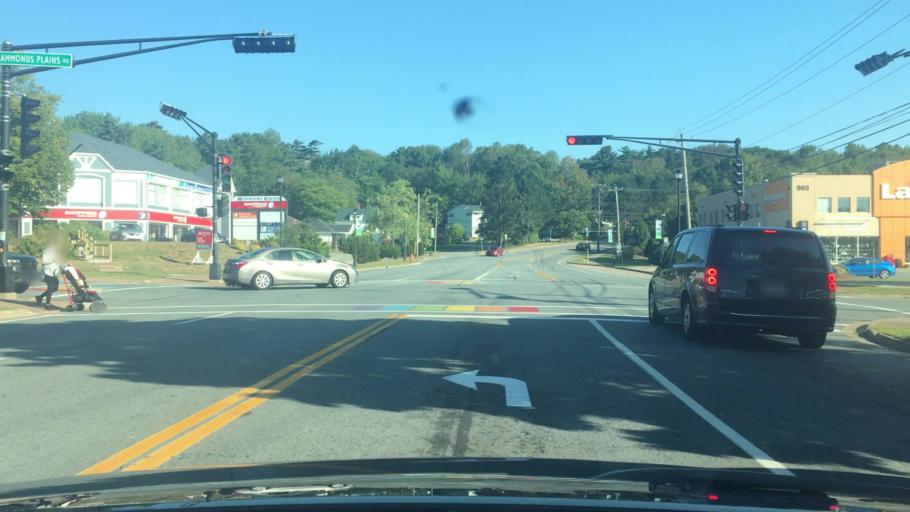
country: CA
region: Nova Scotia
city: Dartmouth
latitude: 44.7150
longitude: -63.6781
